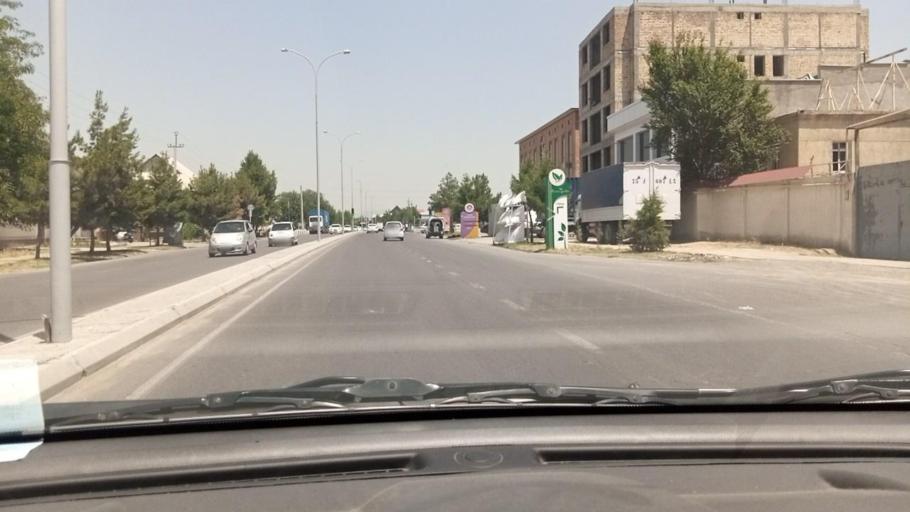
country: UZ
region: Toshkent Shahri
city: Tashkent
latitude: 41.2268
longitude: 69.1802
